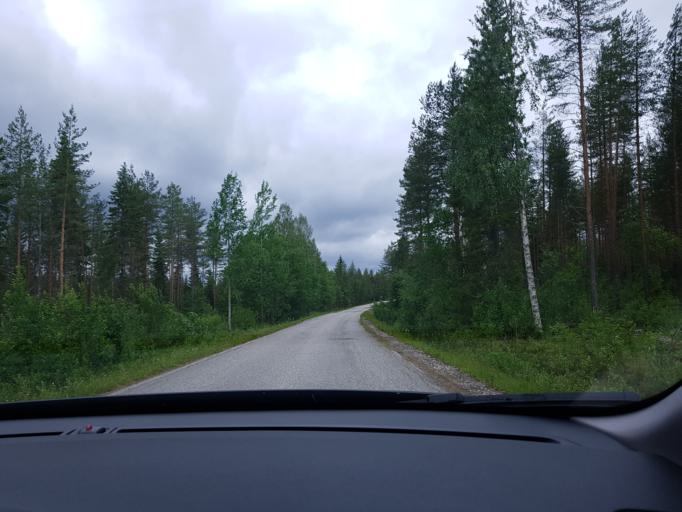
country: FI
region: Kainuu
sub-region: Kehys-Kainuu
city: Kuhmo
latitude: 64.1276
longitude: 29.4643
